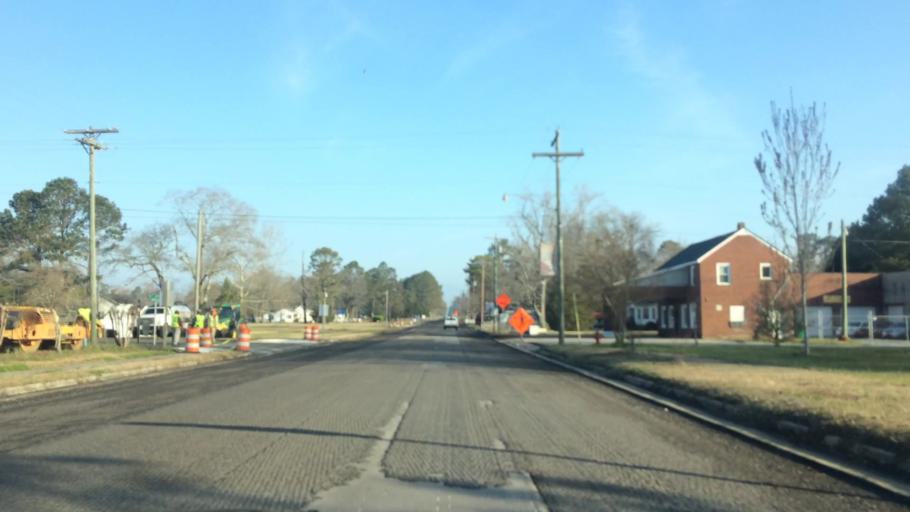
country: US
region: North Carolina
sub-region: Pitt County
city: Farmville
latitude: 35.6745
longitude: -77.6400
